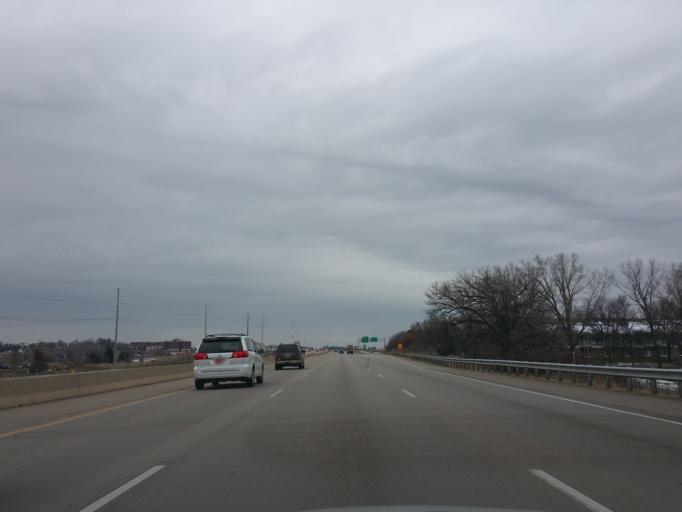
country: US
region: Wisconsin
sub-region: Dane County
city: Maple Bluff
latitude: 43.1443
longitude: -89.3010
